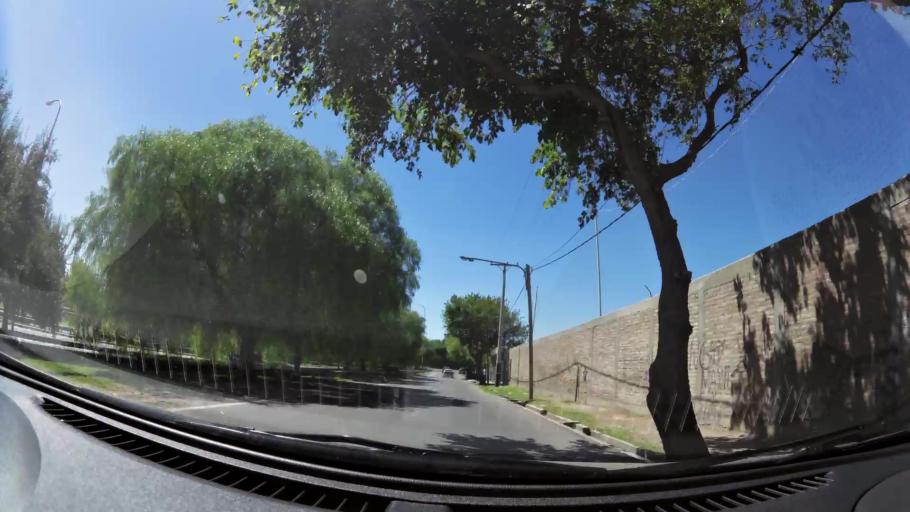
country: AR
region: San Juan
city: San Juan
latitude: -31.5181
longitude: -68.5306
